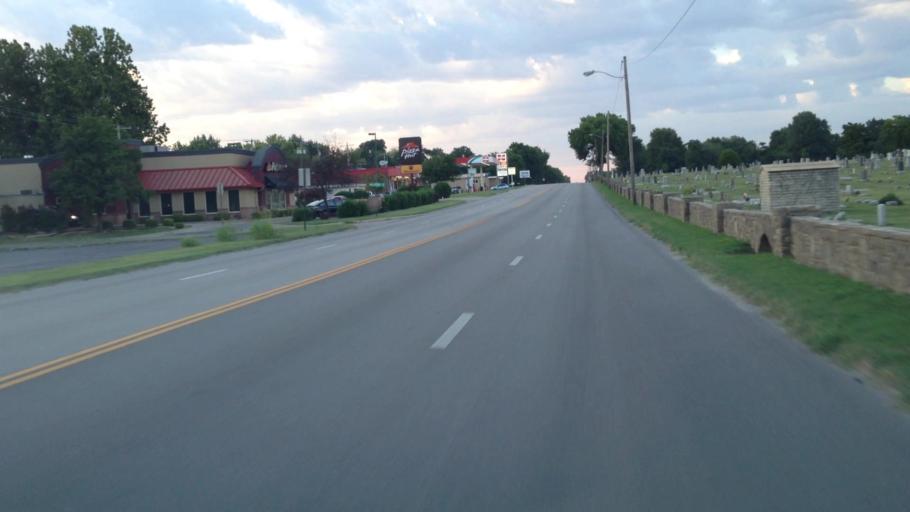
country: US
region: Kansas
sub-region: Montgomery County
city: Independence
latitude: 37.2421
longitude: -95.7062
